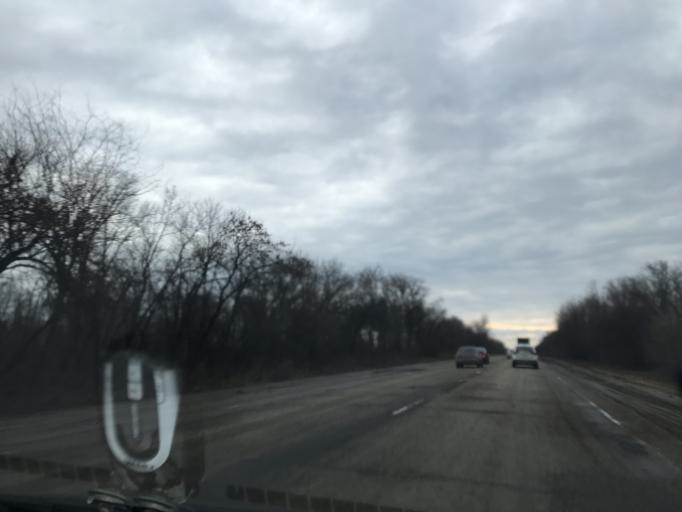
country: RU
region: Krasnodarskiy
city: Mirskoy
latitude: 45.6033
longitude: 40.3907
